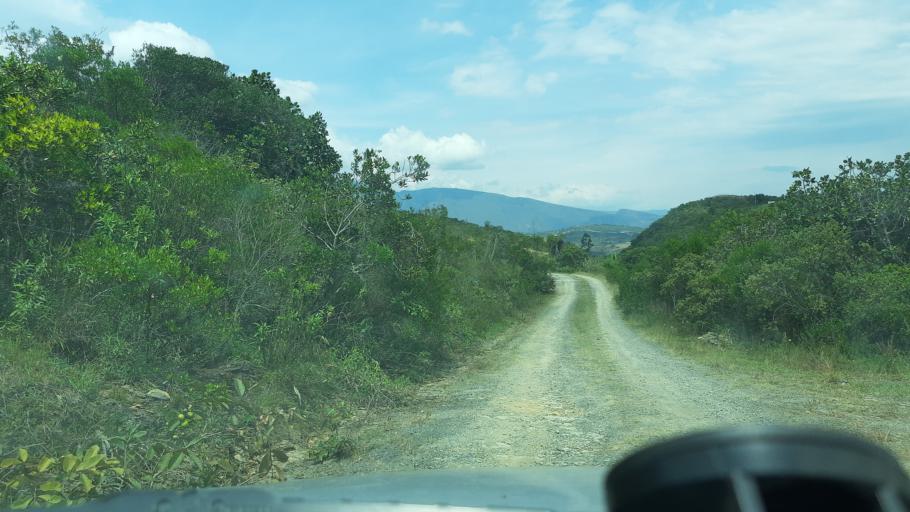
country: CO
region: Boyaca
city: Santa Sofia
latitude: 5.7014
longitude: -73.5805
